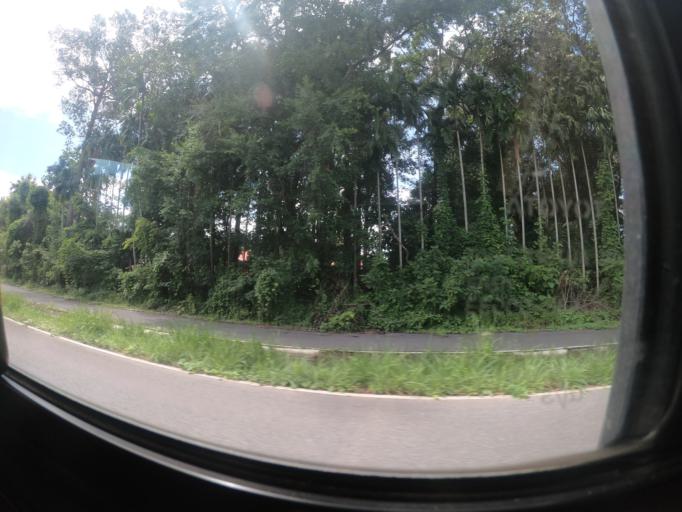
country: TH
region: Nakhon Nayok
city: Nakhon Nayok
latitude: 14.3057
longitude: 101.3113
